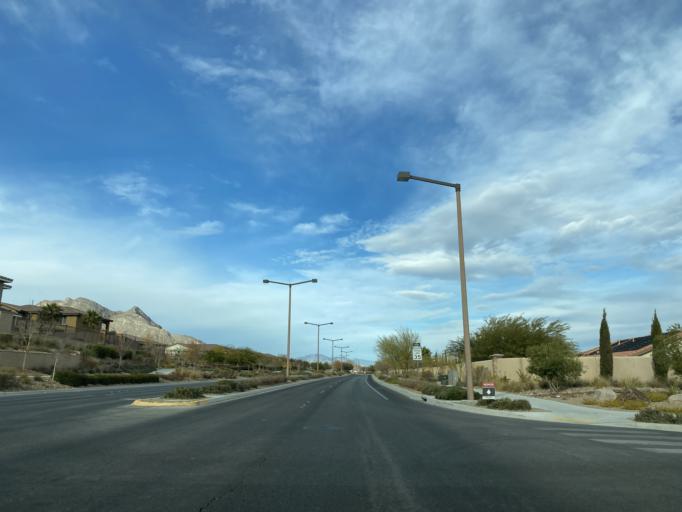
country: US
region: Nevada
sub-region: Clark County
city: Summerlin South
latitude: 36.1773
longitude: -115.3549
